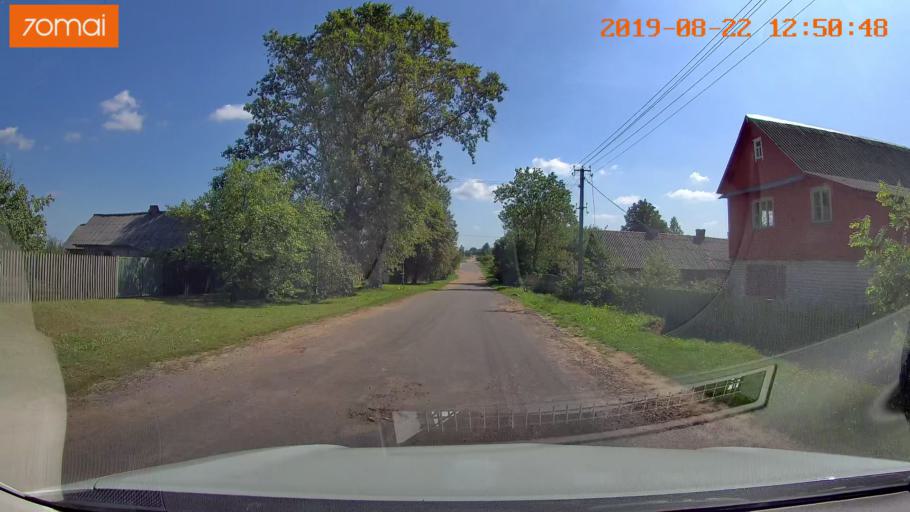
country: BY
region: Minsk
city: Prawdzinski
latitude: 53.4610
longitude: 27.6460
